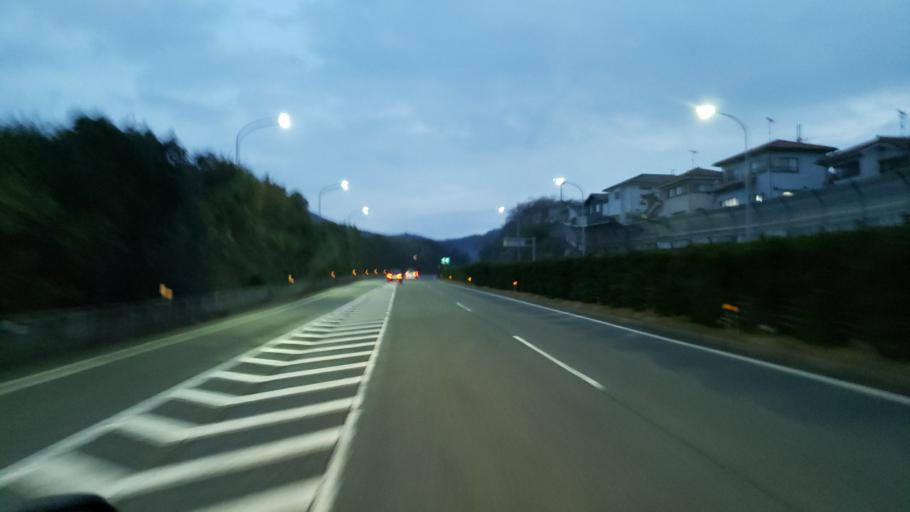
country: JP
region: Hyogo
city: Himeji
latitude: 34.8715
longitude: 134.7393
